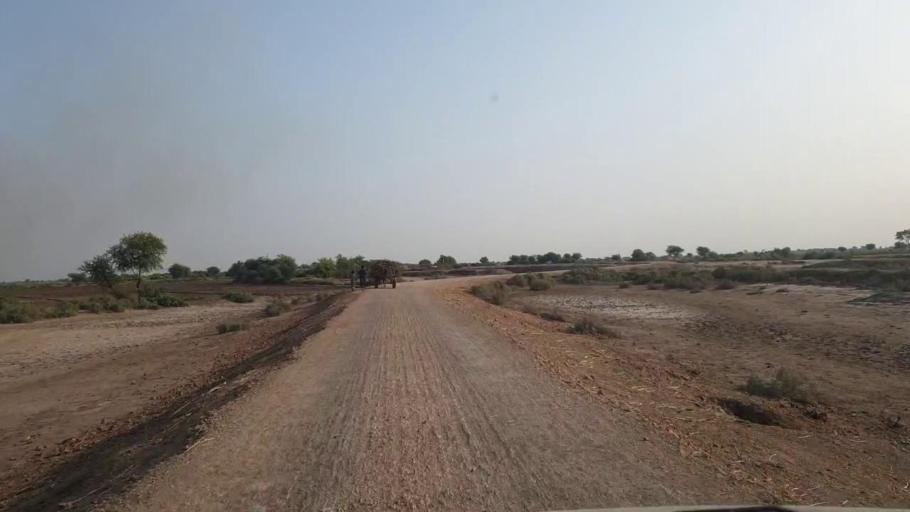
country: PK
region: Sindh
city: Rajo Khanani
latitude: 25.0251
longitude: 68.7801
